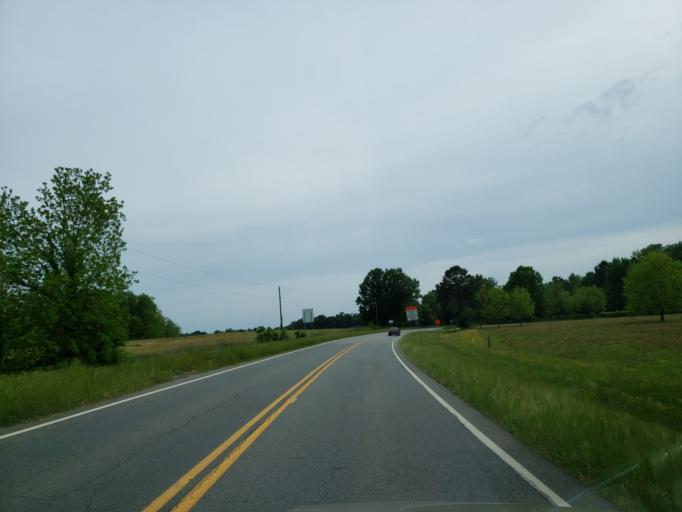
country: US
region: Georgia
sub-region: Macon County
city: Marshallville
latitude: 32.3895
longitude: -83.8673
